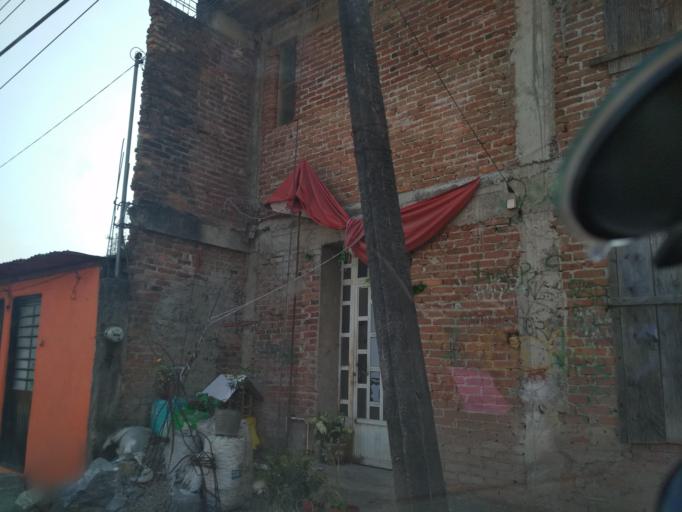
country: MX
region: Veracruz
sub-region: Ixhuatlancillo
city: Fraccionamiento Valle Dorado
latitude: 18.8647
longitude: -97.1166
